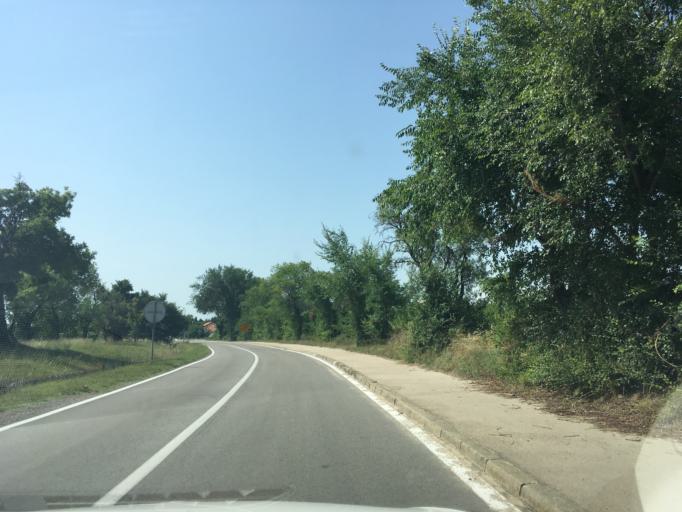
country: HR
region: Zadarska
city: Benkovac
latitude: 44.0269
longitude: 15.6145
